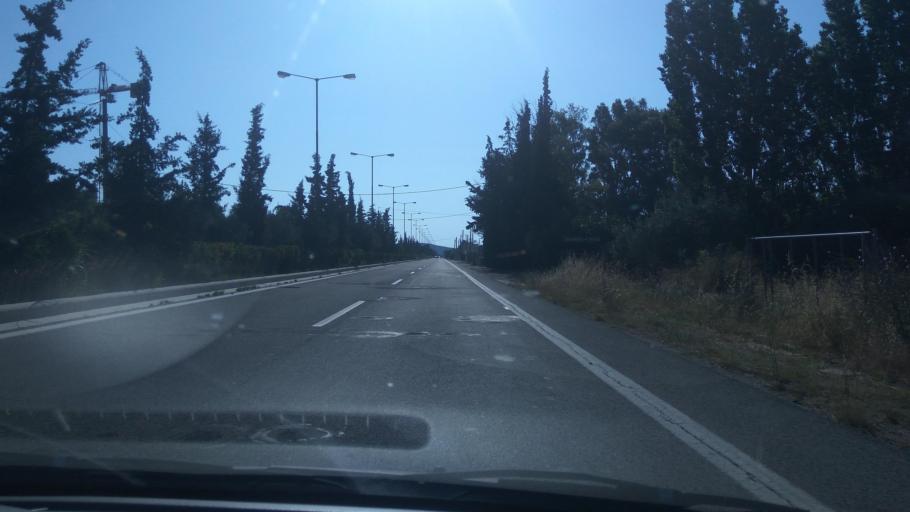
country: GR
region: Attica
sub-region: Nomarchia Anatolikis Attikis
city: Keratea
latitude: 37.8017
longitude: 24.0161
